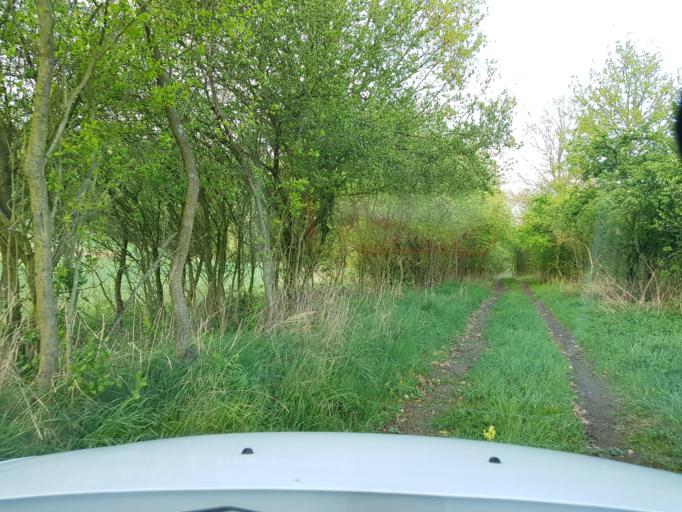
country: PL
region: West Pomeranian Voivodeship
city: Trzcinsko Zdroj
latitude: 52.9892
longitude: 14.6361
